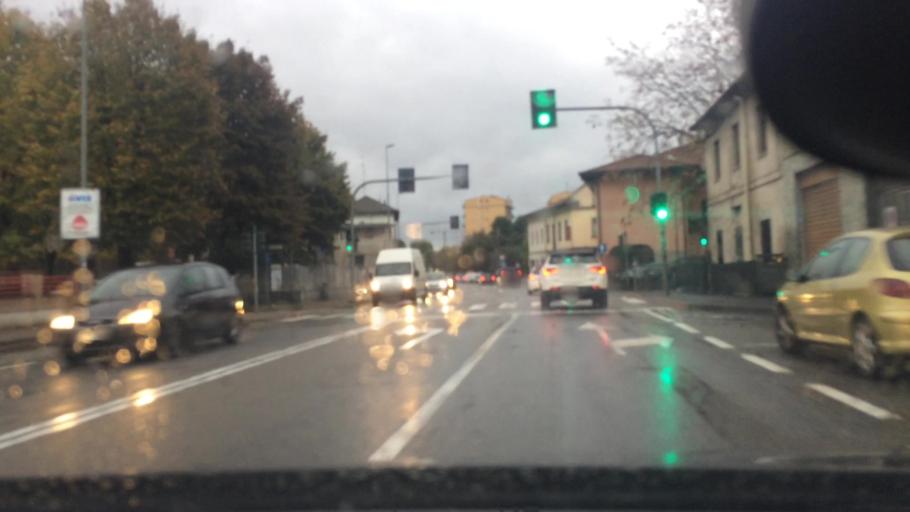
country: IT
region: Lombardy
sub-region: Citta metropolitana di Milano
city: Pogliano Milanese
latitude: 45.5442
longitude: 9.0043
